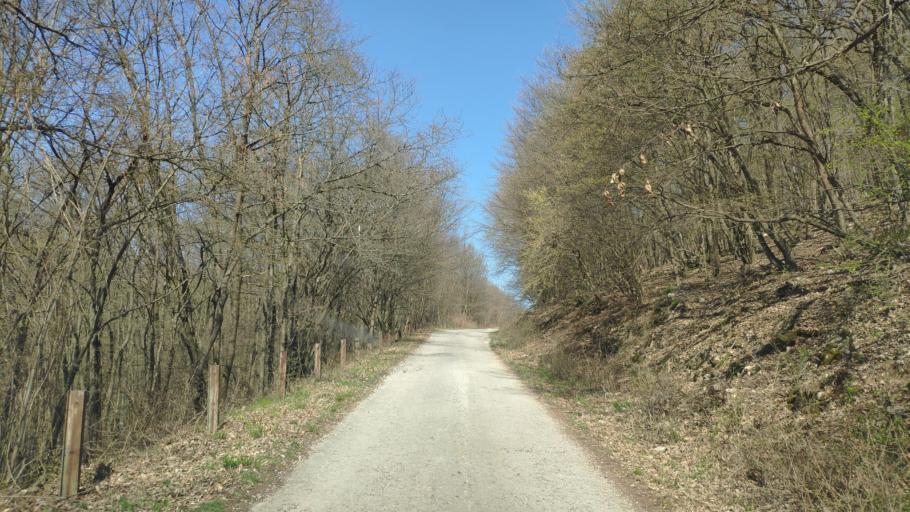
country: SK
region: Kosicky
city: Roznava
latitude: 48.5605
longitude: 20.4048
